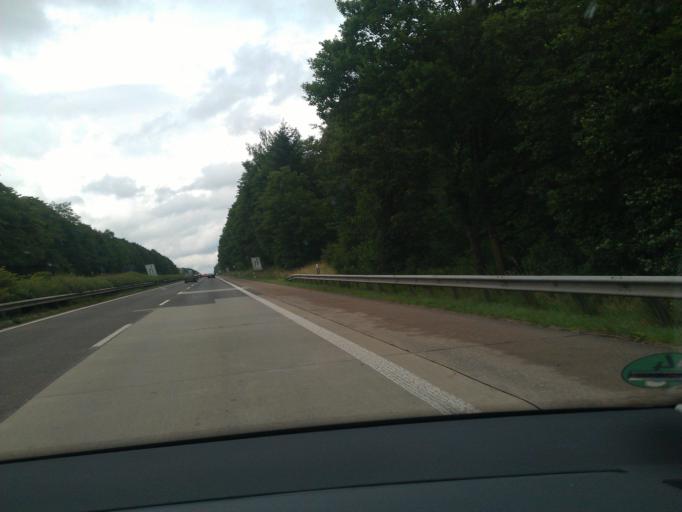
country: DE
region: Rheinland-Pfalz
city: Fohren
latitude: 49.8409
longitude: 6.7758
